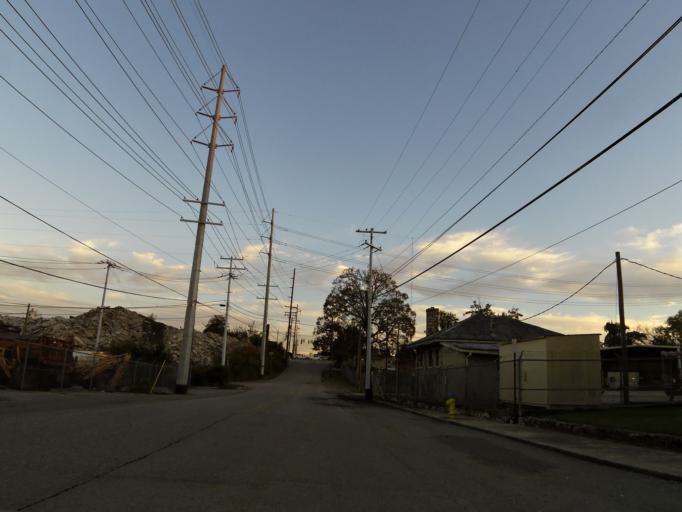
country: US
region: Tennessee
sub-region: Knox County
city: Knoxville
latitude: 35.9587
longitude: -83.9525
